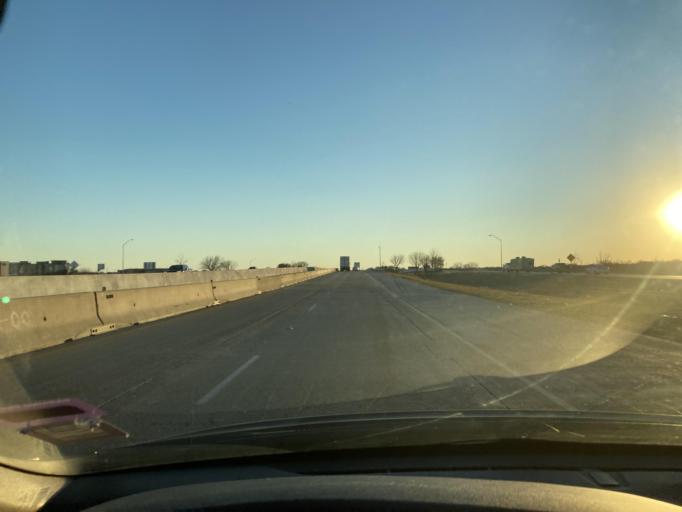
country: US
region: Texas
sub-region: Ellis County
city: Waxahachie
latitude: 32.4292
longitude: -96.8614
